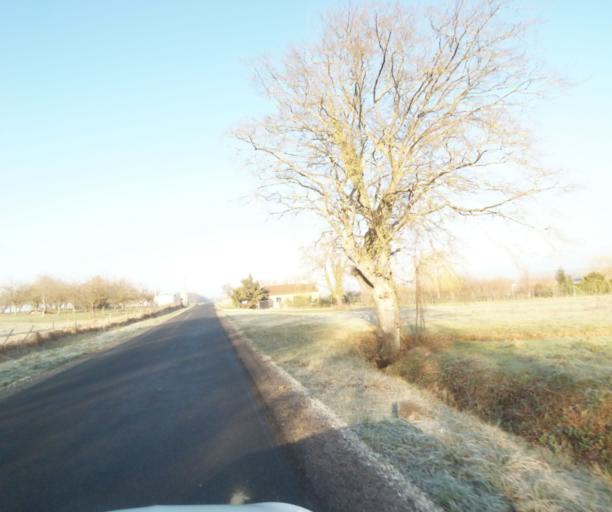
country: FR
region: Champagne-Ardenne
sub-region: Departement de la Haute-Marne
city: Montier-en-Der
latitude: 48.4831
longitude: 4.7472
